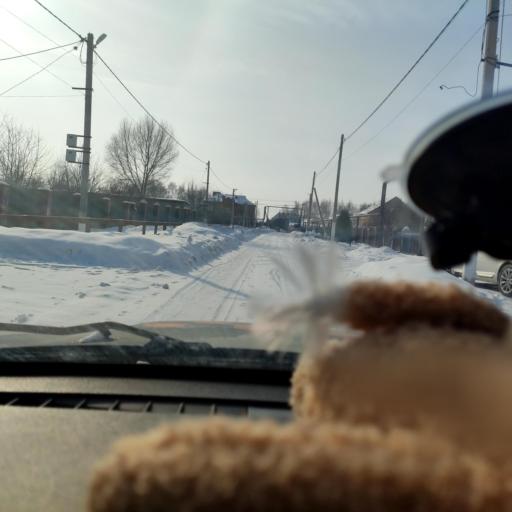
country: RU
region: Samara
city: Podstepki
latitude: 53.5121
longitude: 49.1200
